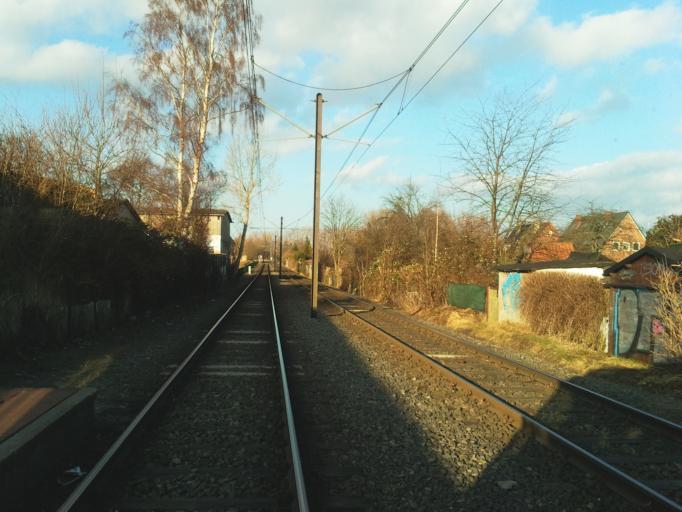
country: DE
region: Mecklenburg-Vorpommern
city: Kritzmow
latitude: 54.1071
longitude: 12.0790
